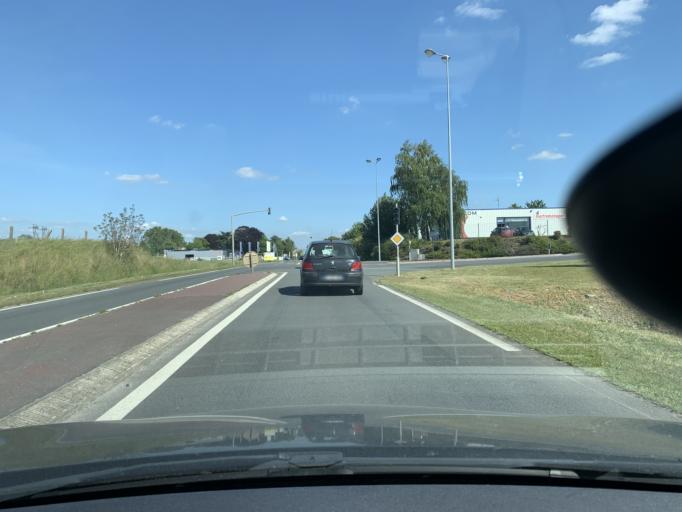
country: FR
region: Nord-Pas-de-Calais
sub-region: Departement du Nord
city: Caudry
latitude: 50.1339
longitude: 3.4126
